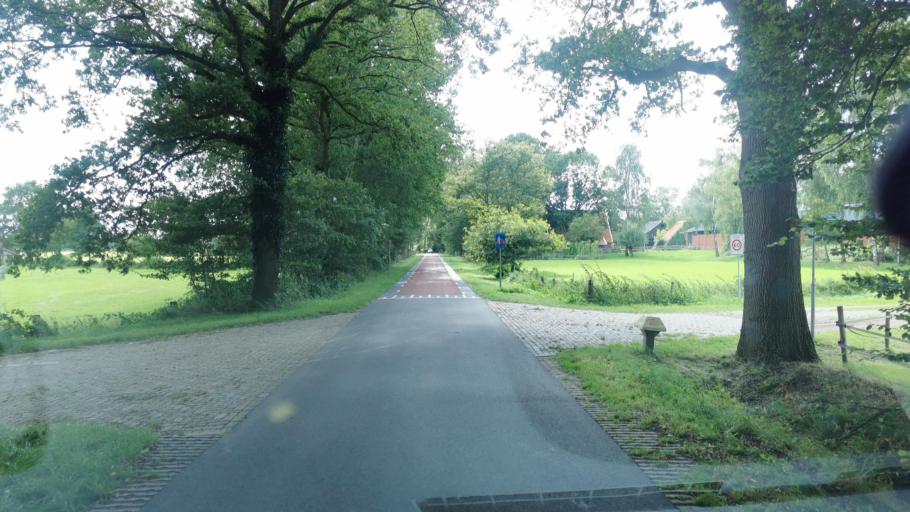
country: NL
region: Overijssel
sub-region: Gemeente Losser
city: Losser
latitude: 52.2559
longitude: 6.9899
